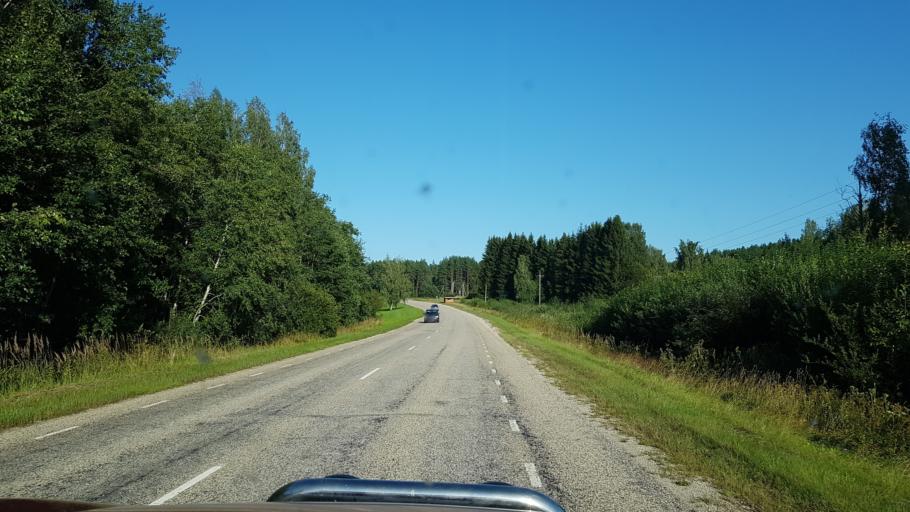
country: EE
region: Vorumaa
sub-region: Voru linn
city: Voru
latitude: 57.8141
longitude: 27.3132
